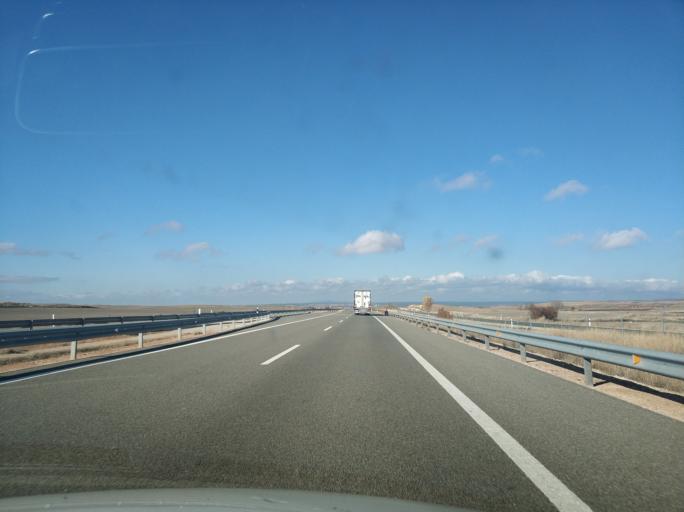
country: ES
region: Castille and Leon
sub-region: Provincia de Soria
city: Coscurita
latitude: 41.4036
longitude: -2.4791
